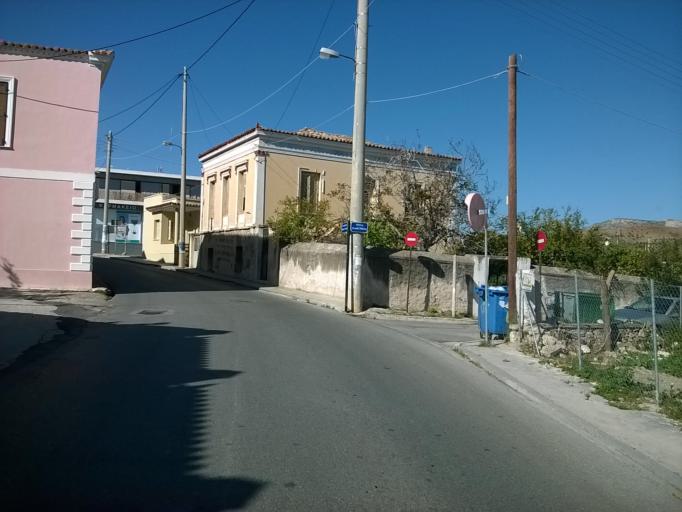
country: GR
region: Attica
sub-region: Nomarchia Anatolikis Attikis
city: Keratea
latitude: 37.8081
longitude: 23.9803
